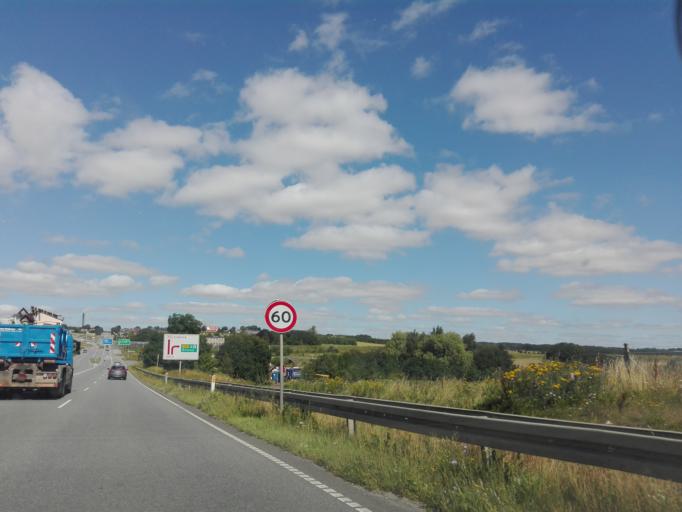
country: DK
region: Central Jutland
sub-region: Arhus Kommune
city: Trige
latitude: 56.2096
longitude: 10.1743
